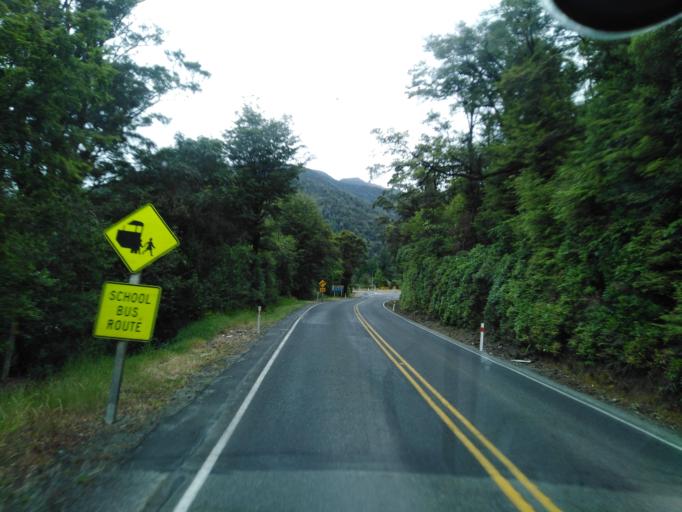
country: NZ
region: Tasman
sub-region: Tasman District
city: Wakefield
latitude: -41.7115
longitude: 172.5593
